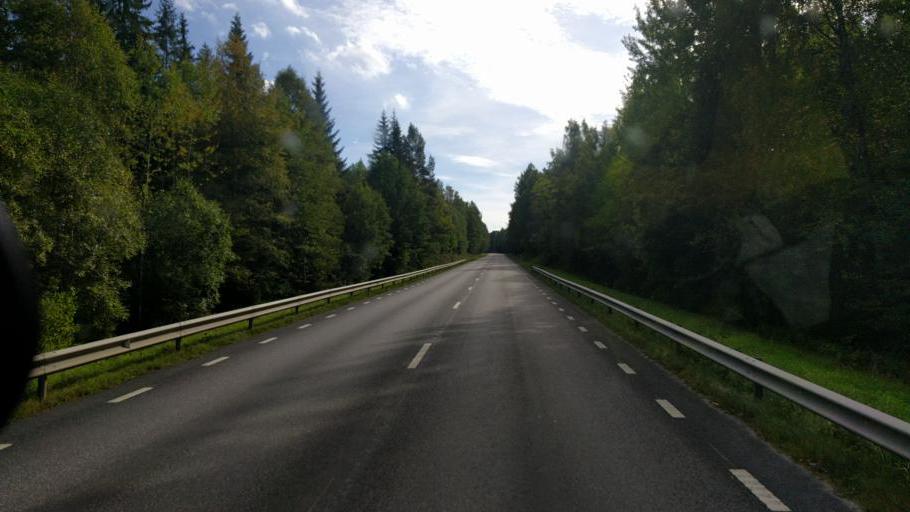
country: SE
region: OEstergoetland
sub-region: Kinda Kommun
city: Kisa
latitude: 57.9448
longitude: 15.6667
